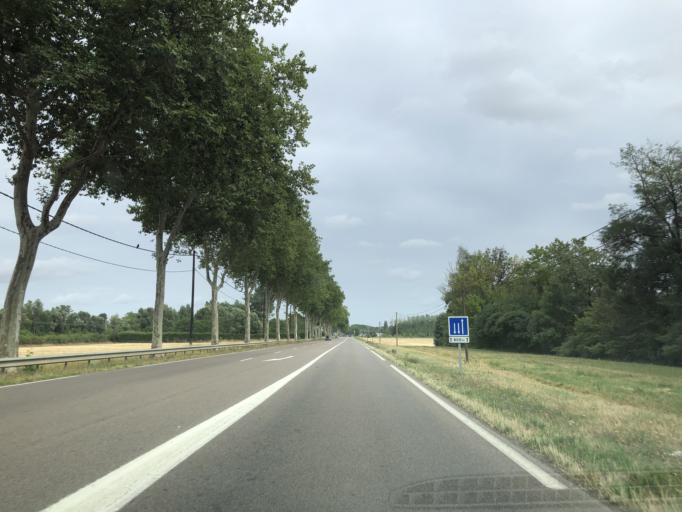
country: FR
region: Bourgogne
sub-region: Departement de l'Yonne
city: Joigny
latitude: 47.9626
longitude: 3.4338
